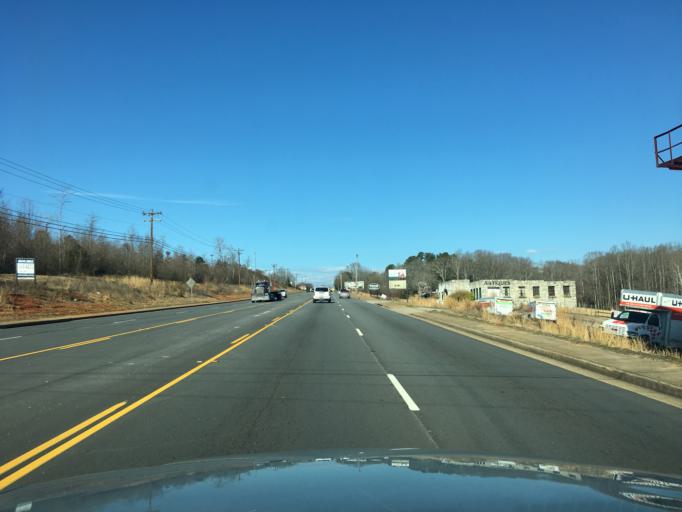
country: US
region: South Carolina
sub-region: Pickens County
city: Pickens
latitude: 34.8748
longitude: -82.6969
